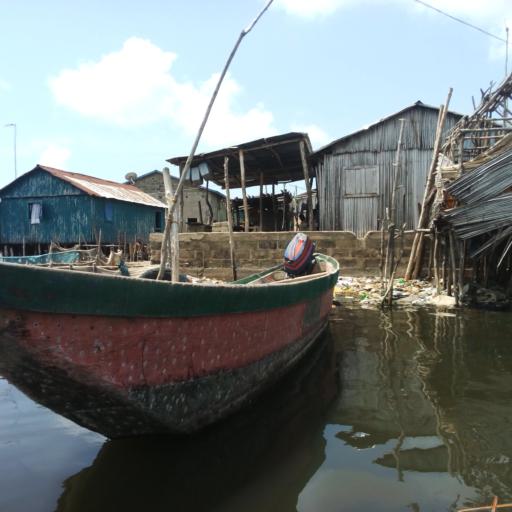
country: BJ
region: Littoral
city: Cotonou
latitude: 6.3934
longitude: 2.4311
